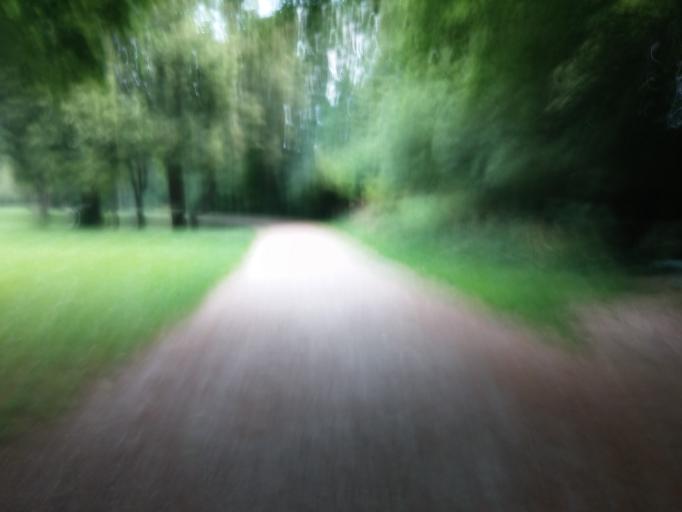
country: DE
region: Bavaria
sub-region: Upper Bavaria
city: Bogenhausen
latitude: 48.1600
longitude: 11.6350
